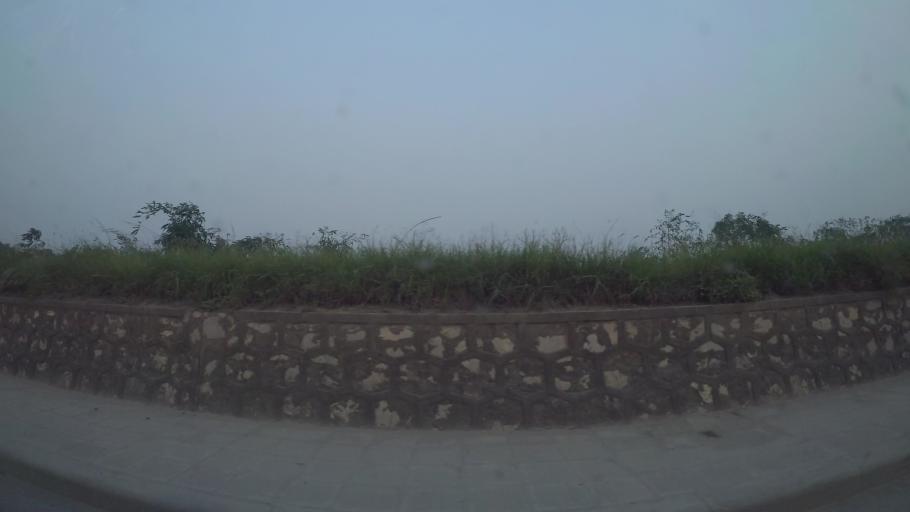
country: VN
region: Hung Yen
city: Van Giang
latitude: 20.9771
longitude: 105.8904
